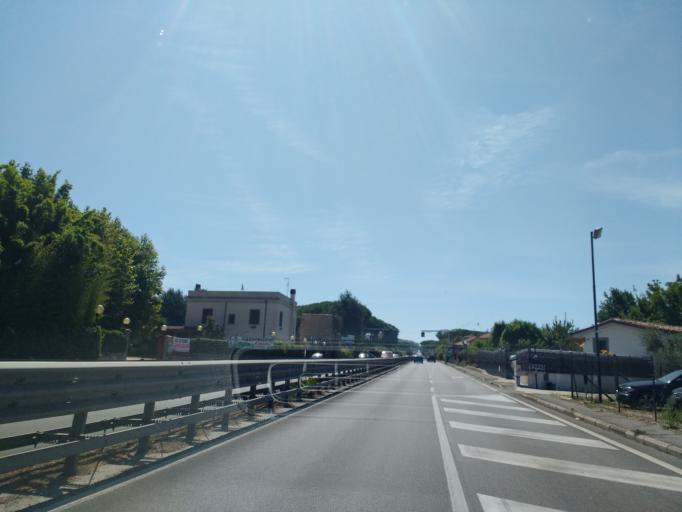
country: IT
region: Latium
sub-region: Citta metropolitana di Roma Capitale
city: Marino
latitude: 41.7613
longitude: 12.6221
